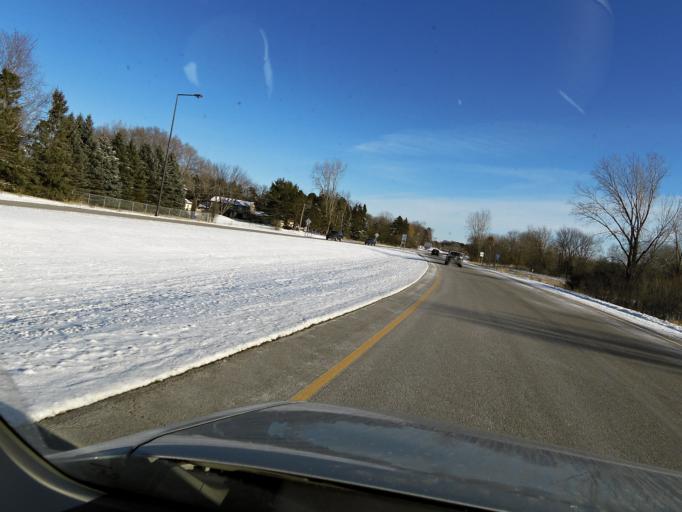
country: US
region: Minnesota
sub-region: Washington County
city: Lake Elmo
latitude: 44.9966
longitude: -92.9225
